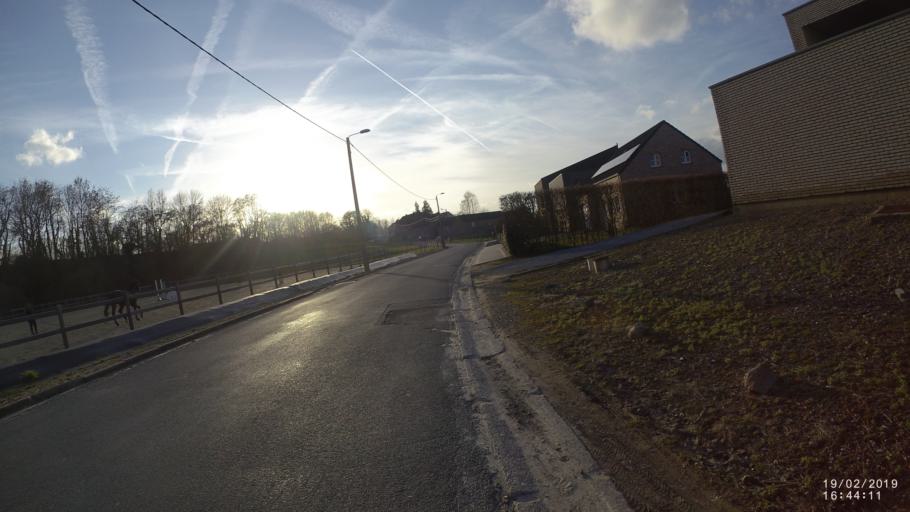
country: BE
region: Flanders
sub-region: Provincie Limburg
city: Borgloon
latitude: 50.8099
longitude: 5.3292
